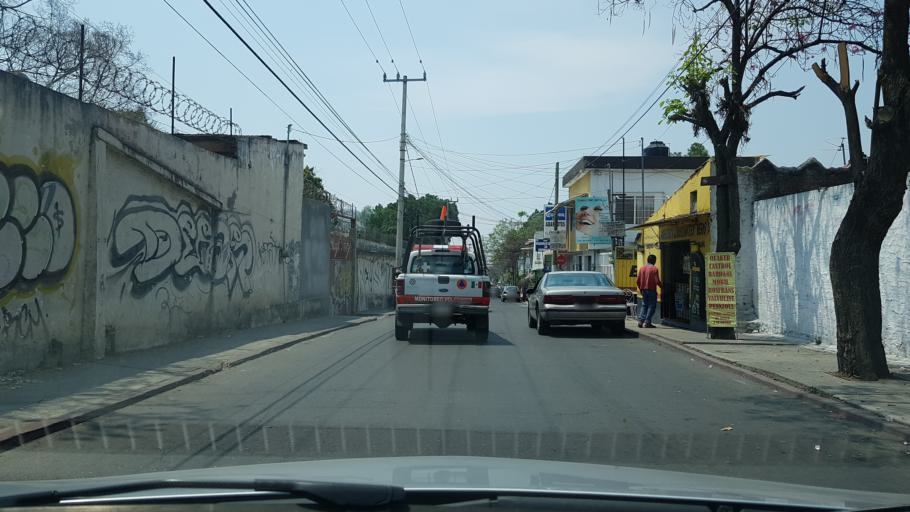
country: MX
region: Morelos
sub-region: Jiutepec
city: Jiutepec
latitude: 18.8878
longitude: -99.1762
